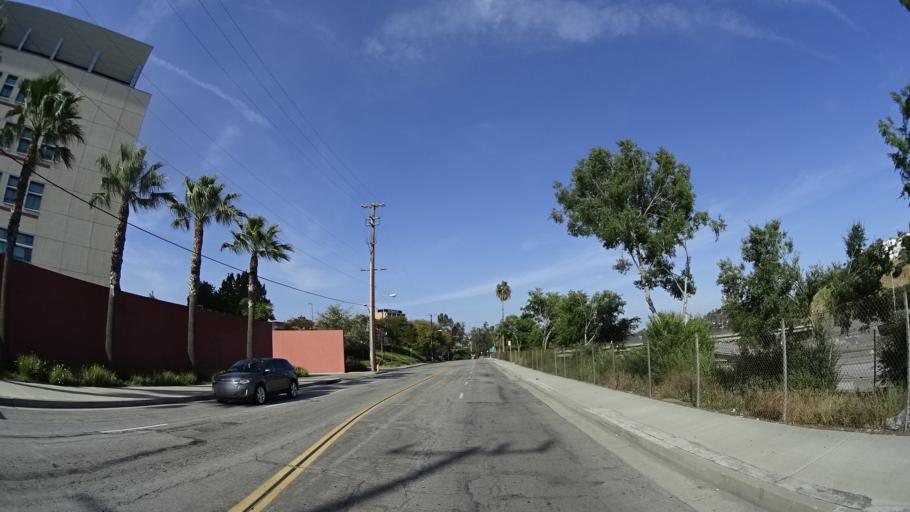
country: US
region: California
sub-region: Los Angeles County
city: Belvedere
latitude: 34.0615
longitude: -118.1734
